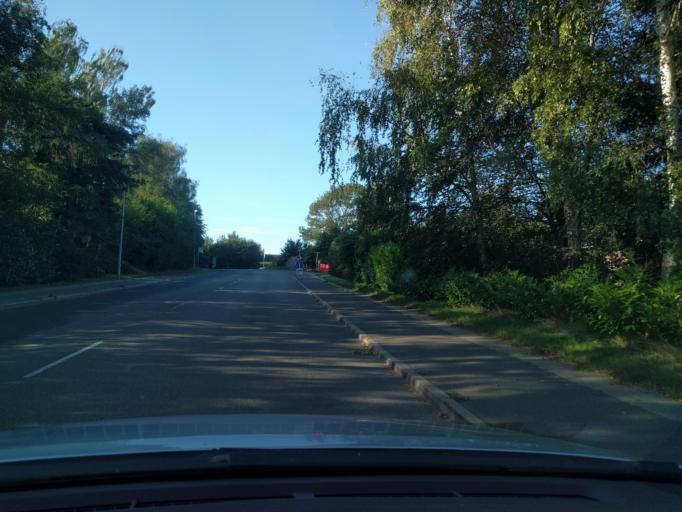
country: DK
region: Central Jutland
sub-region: Horsens Kommune
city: Horsens
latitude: 55.8692
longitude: 9.8988
